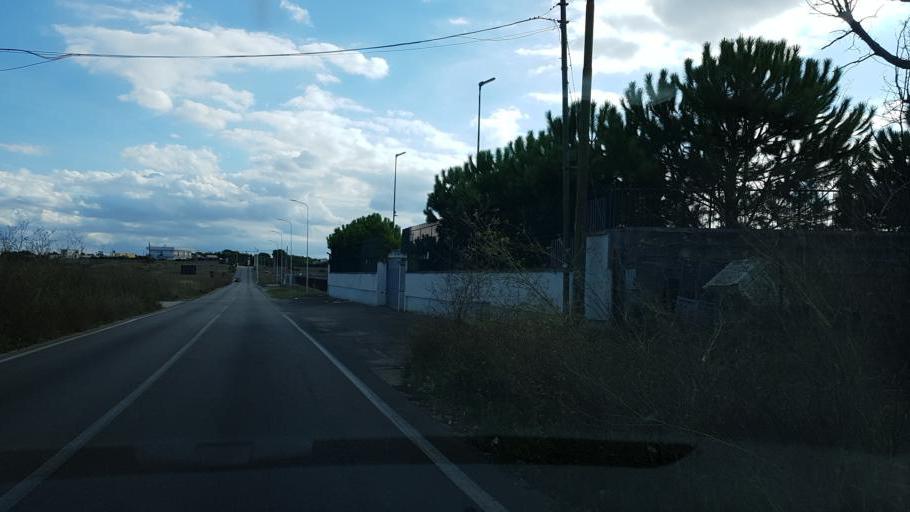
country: IT
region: Apulia
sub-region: Provincia di Lecce
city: Nardo
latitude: 40.1506
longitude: 18.0179
